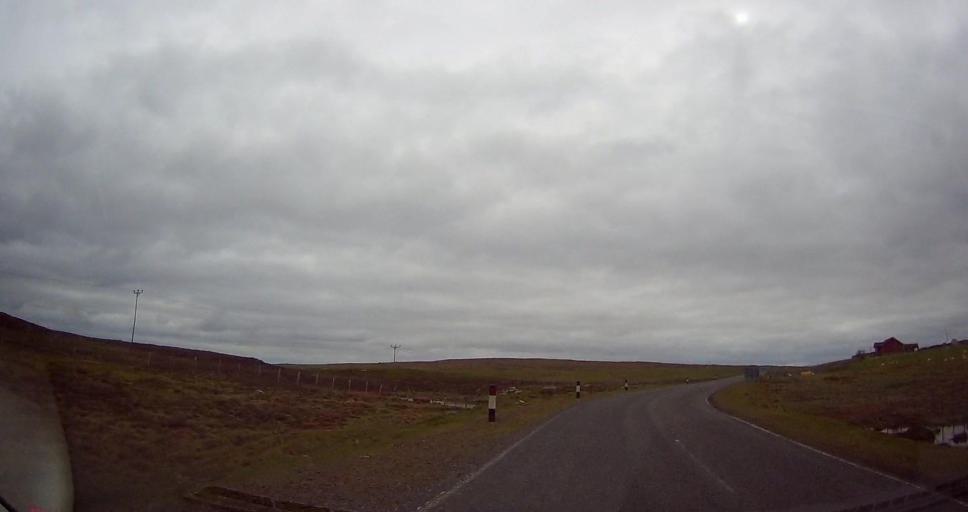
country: GB
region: Scotland
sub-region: Shetland Islands
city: Shetland
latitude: 60.6958
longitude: -0.9234
